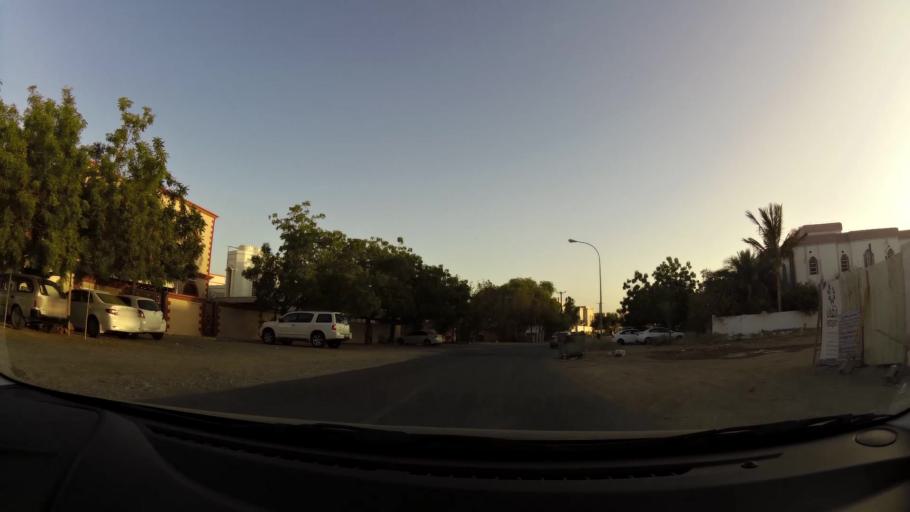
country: OM
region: Muhafazat Masqat
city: As Sib al Jadidah
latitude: 23.6032
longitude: 58.2302
